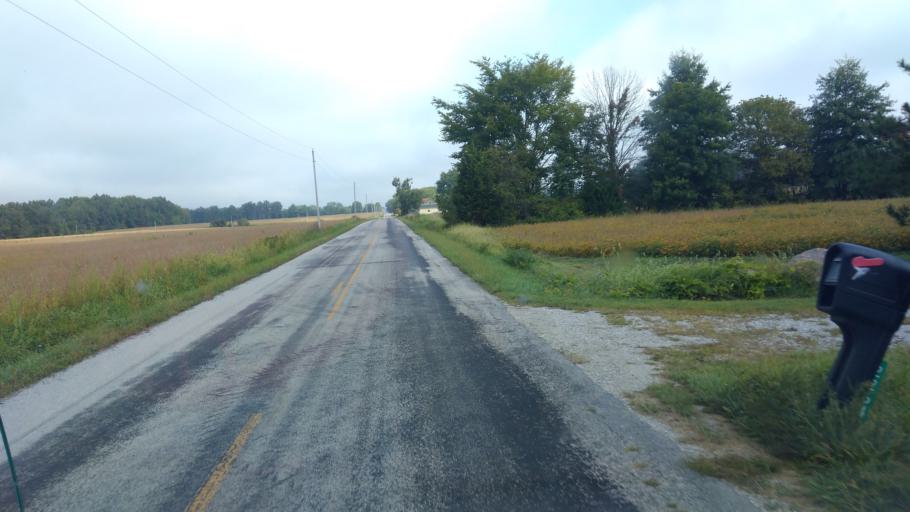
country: US
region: Ohio
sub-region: Morrow County
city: Cardington
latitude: 40.5462
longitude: -82.9767
